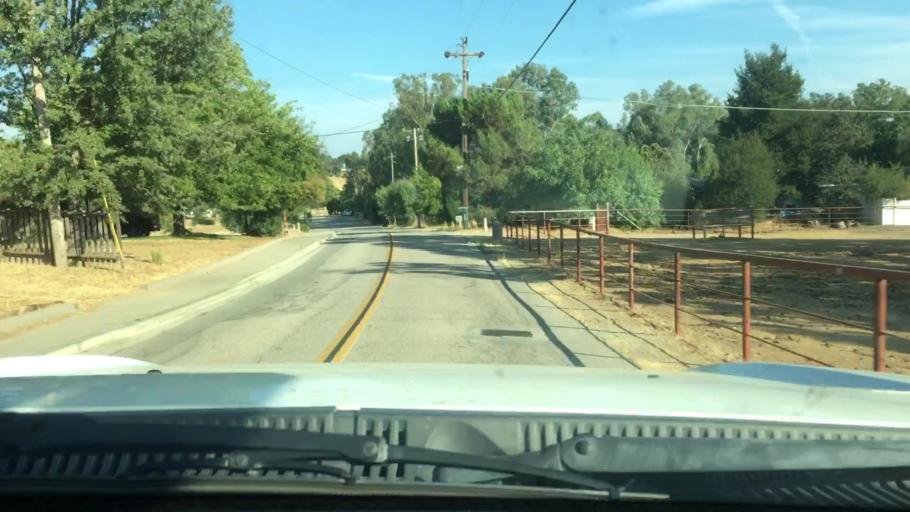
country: US
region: California
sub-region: San Luis Obispo County
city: Atascadero
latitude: 35.4614
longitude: -120.6737
